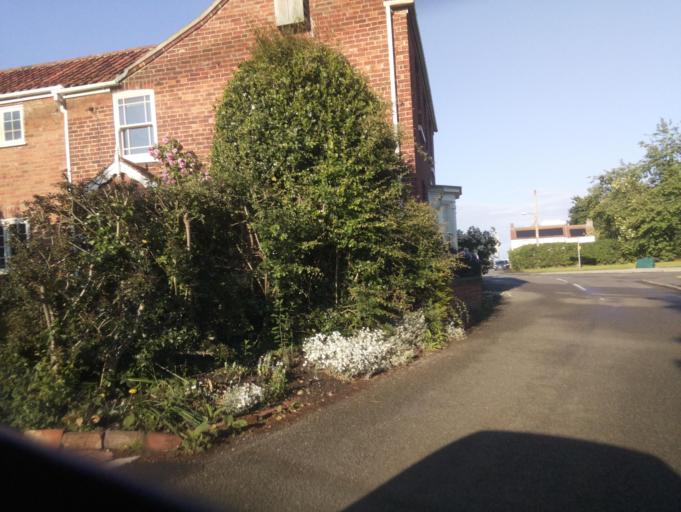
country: GB
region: England
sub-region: Lincolnshire
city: Skellingthorpe
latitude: 53.1292
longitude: -0.6378
